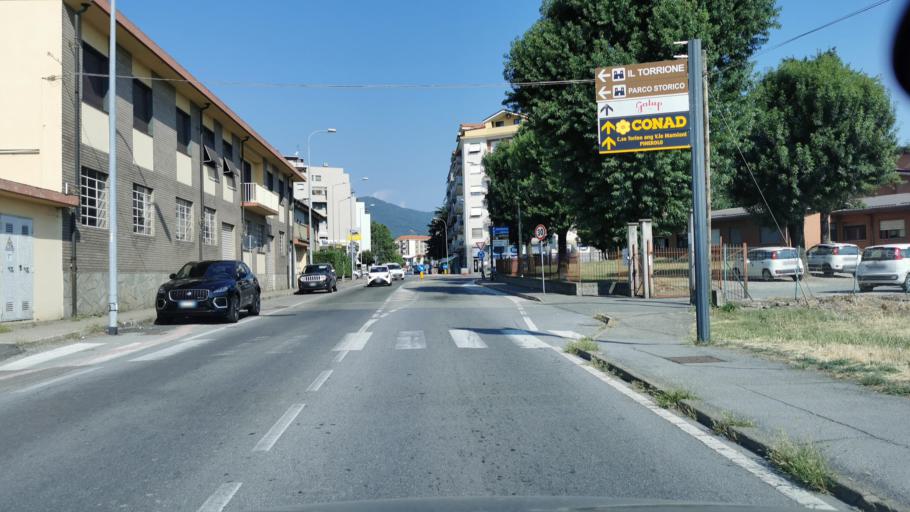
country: IT
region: Piedmont
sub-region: Provincia di Torino
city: Pinerolo
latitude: 44.8845
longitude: 7.3467
